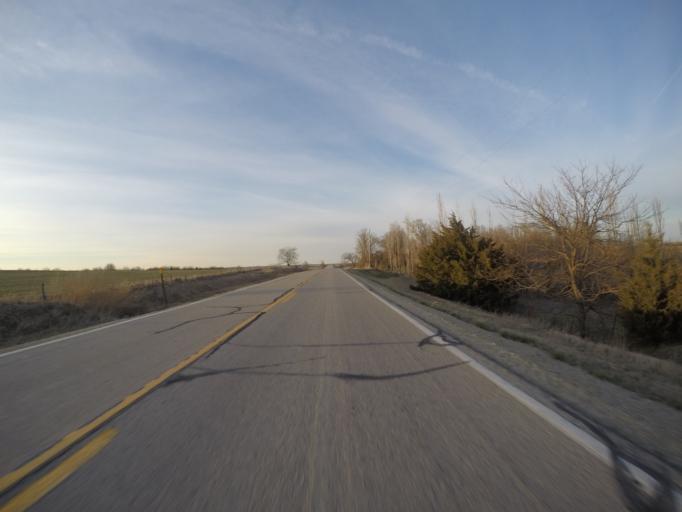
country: US
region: Kansas
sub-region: Riley County
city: Fort Riley North
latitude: 39.3673
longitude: -96.8494
